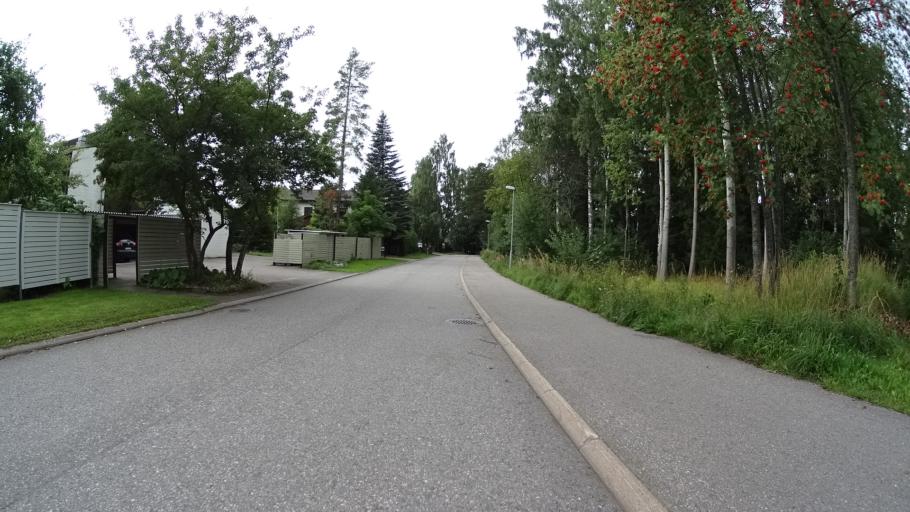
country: FI
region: Uusimaa
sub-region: Helsinki
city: Kilo
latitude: 60.1889
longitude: 24.7861
